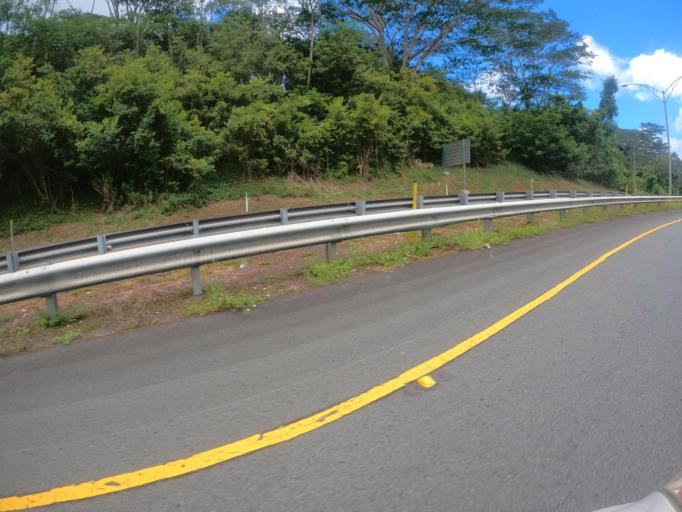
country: US
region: Hawaii
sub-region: Honolulu County
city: Maunawili
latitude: 21.3863
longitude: -157.7897
